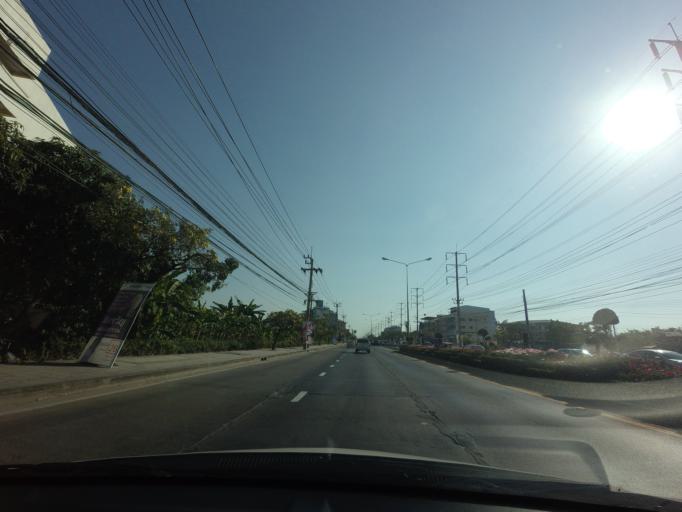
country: TH
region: Bangkok
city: Nong Chok
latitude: 13.8479
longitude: 100.8590
